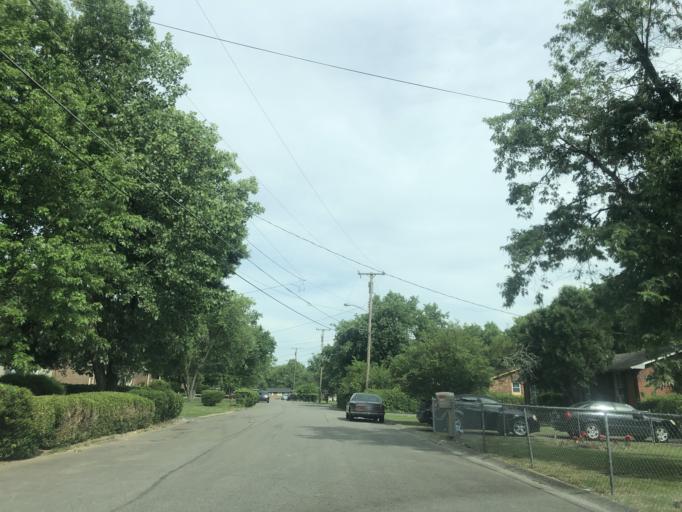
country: US
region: Tennessee
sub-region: Davidson County
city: Nashville
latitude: 36.2207
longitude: -86.8099
